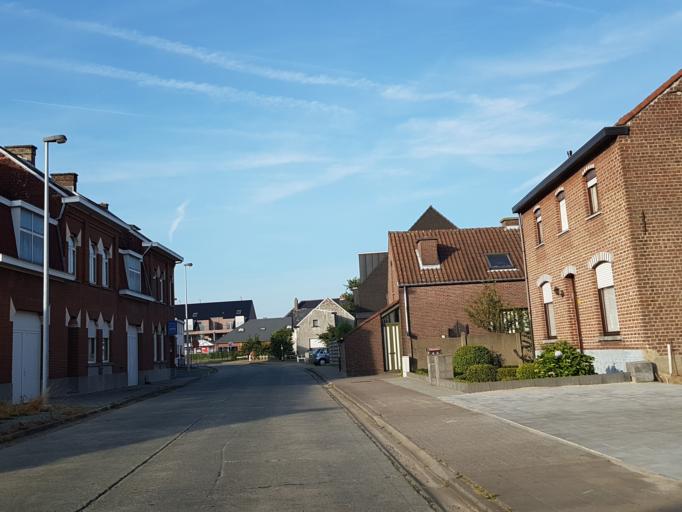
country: BE
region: Flanders
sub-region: Provincie Vlaams-Brabant
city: Opwijk
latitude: 50.9399
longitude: 4.1359
